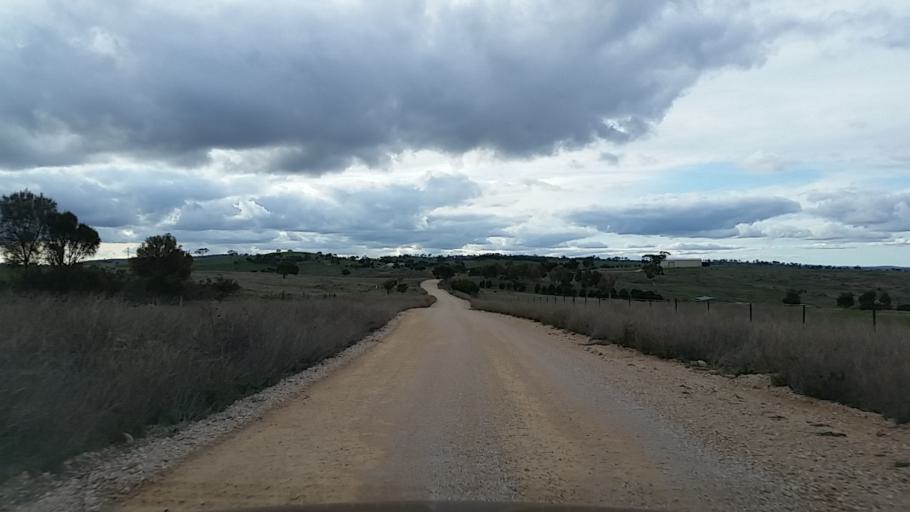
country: AU
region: South Australia
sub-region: Mount Barker
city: Callington
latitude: -34.9826
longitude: 139.0575
